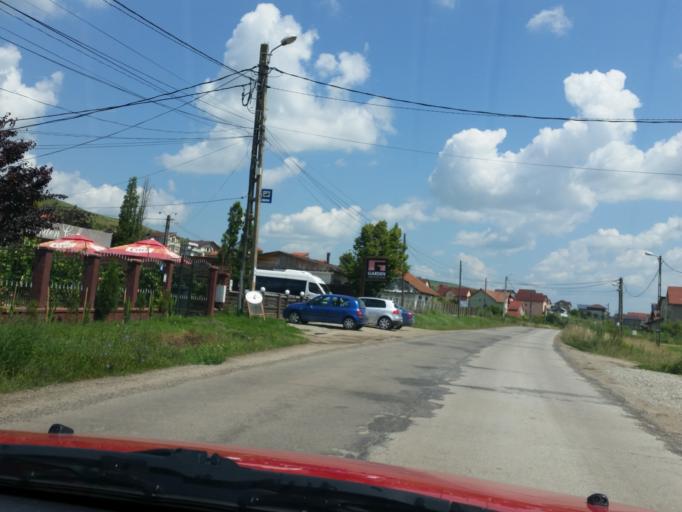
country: RO
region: Cluj
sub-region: Comuna Chinteni
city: Chinteni
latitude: 46.8484
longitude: 23.5541
